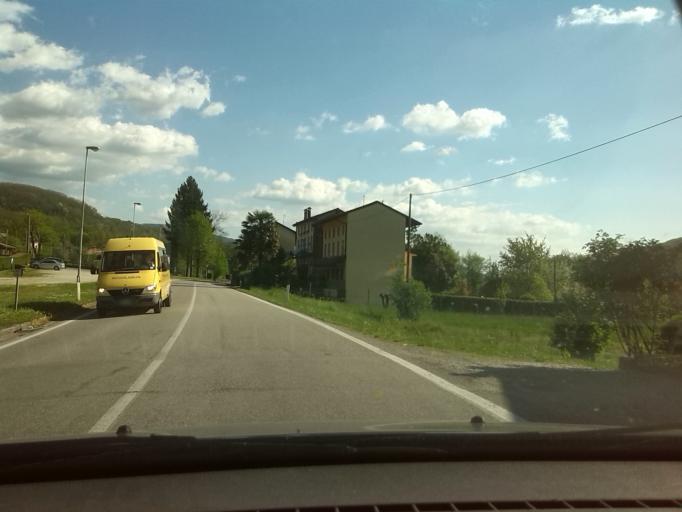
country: IT
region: Friuli Venezia Giulia
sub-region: Provincia di Udine
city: Pulfero
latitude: 46.1484
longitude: 13.4888
